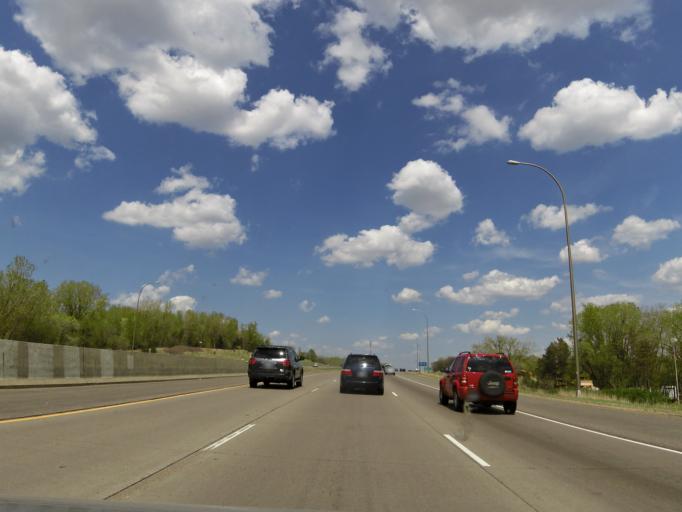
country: US
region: Minnesota
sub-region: Washington County
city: Newport
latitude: 44.9019
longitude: -92.9941
